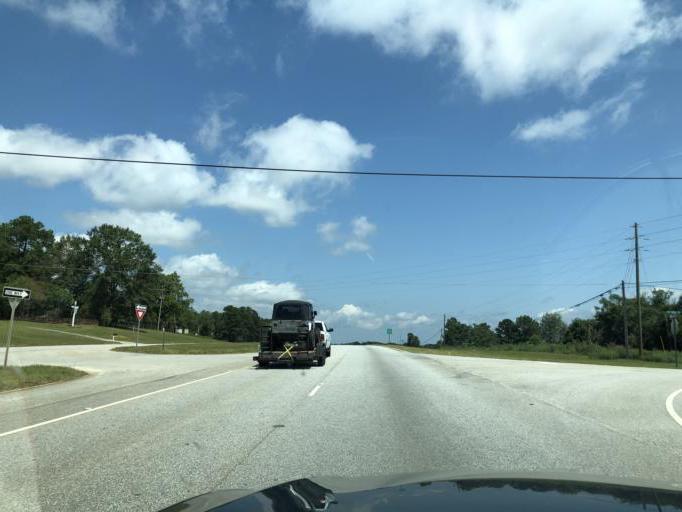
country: US
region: Alabama
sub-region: Barbour County
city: Eufaula
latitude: 31.7793
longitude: -85.1767
